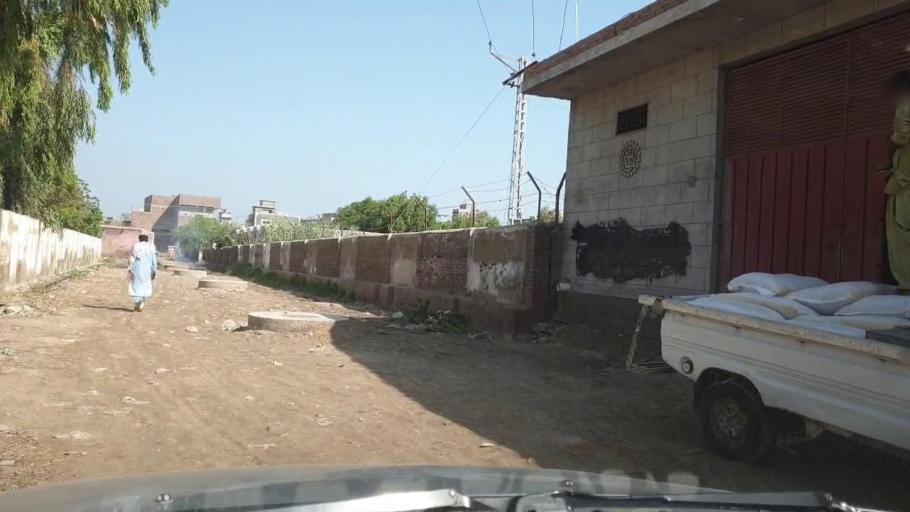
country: PK
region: Sindh
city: Matli
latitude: 25.0425
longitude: 68.6614
